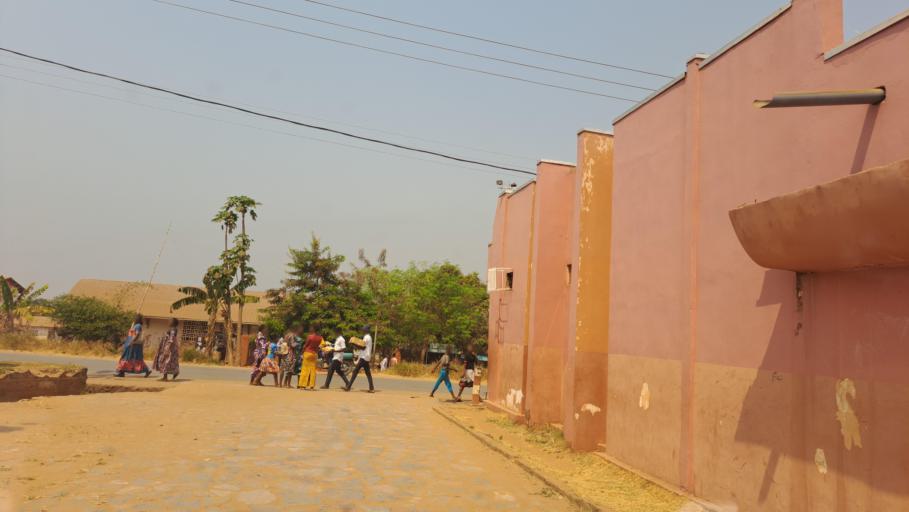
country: CD
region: Kasai-Oriental
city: Mbuji-Mayi
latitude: -6.1267
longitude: 23.6144
